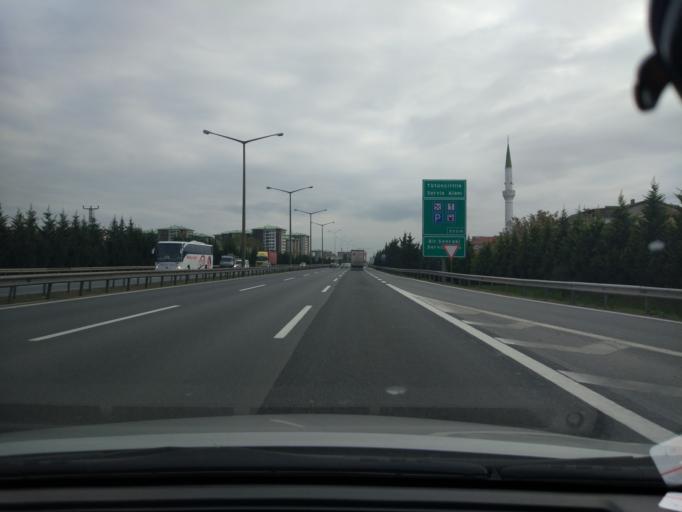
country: TR
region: Kocaeli
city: Korfez
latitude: 40.7702
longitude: 29.7887
